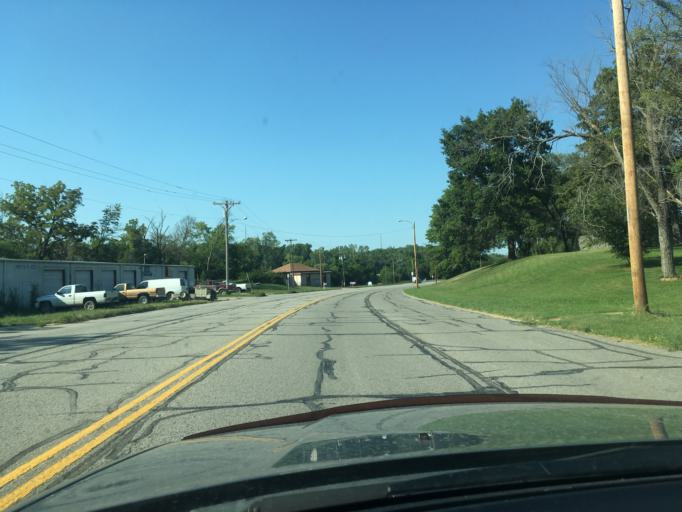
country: US
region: Kansas
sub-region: Atchison County
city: Atchison
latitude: 39.5580
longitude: -95.1485
